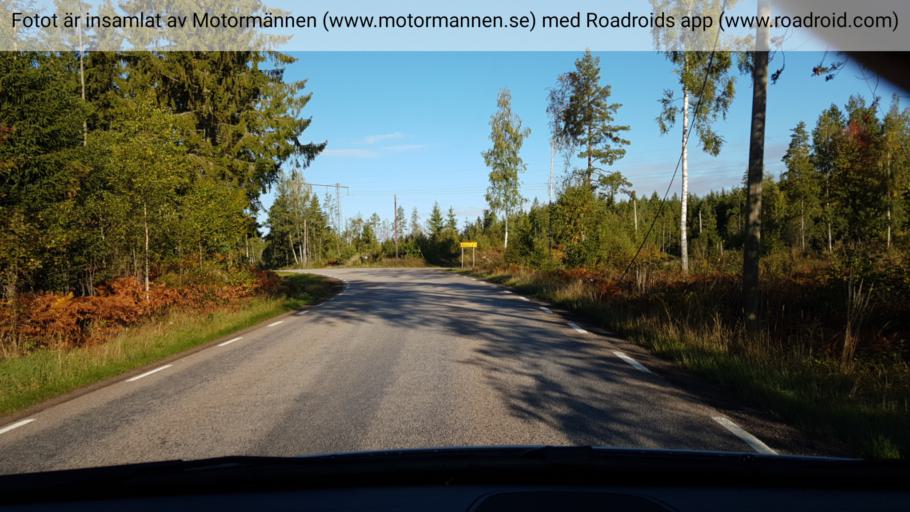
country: SE
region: Vaestra Goetaland
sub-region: Skovde Kommun
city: Stopen
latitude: 58.5401
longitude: 13.6944
